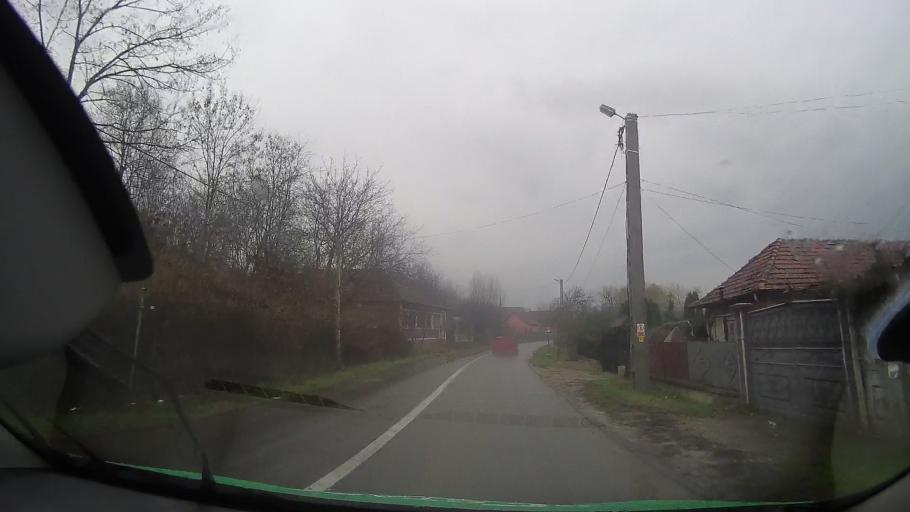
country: RO
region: Bihor
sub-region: Comuna Holod
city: Vintere
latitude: 46.7728
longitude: 22.1365
